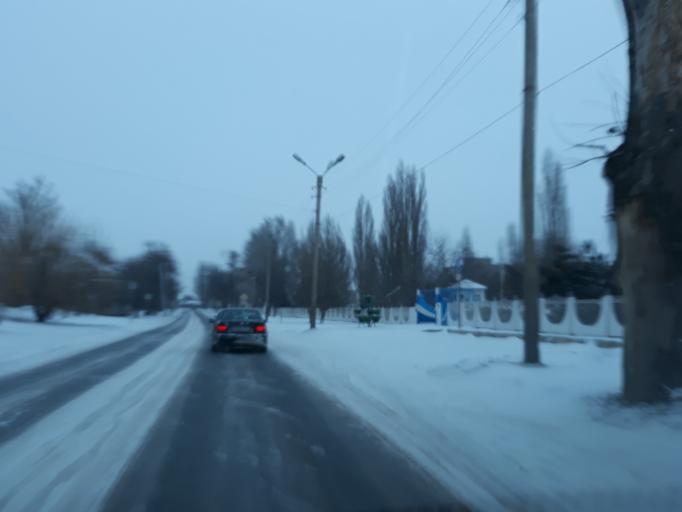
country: RU
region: Rostov
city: Taganrog
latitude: 47.2499
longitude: 38.9336
